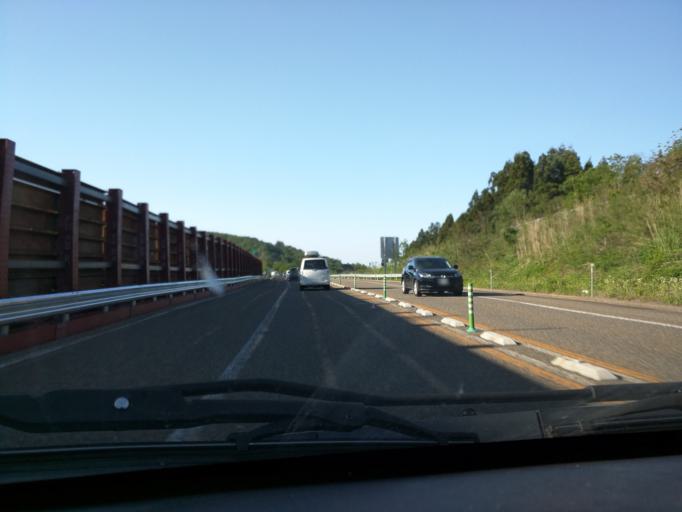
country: JP
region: Niigata
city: Arai
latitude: 37.0366
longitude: 138.2315
